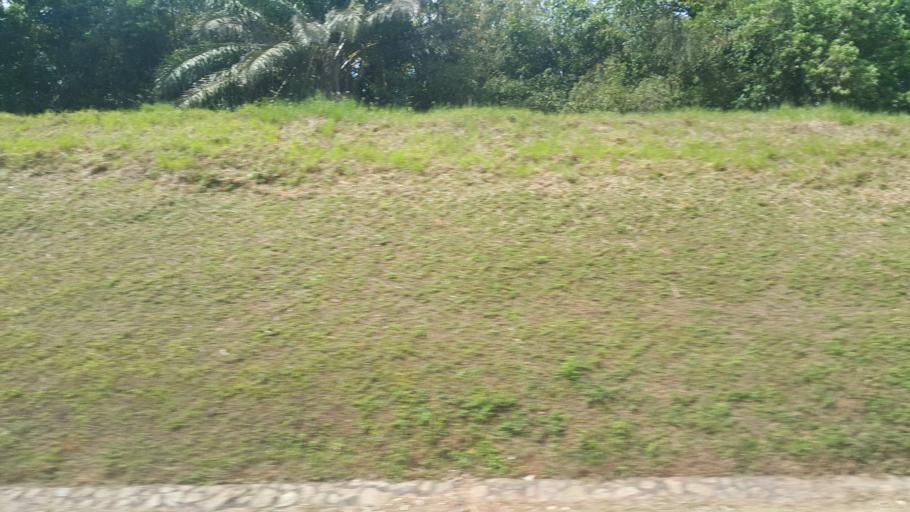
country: MY
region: Johor
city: Bakri
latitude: 2.1410
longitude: 102.7153
